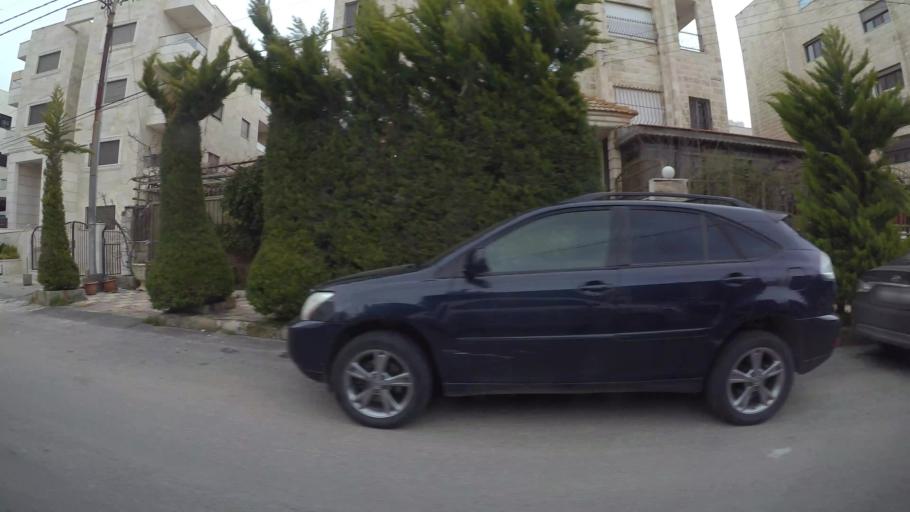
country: JO
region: Amman
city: Al Jubayhah
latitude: 31.9959
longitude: 35.8456
